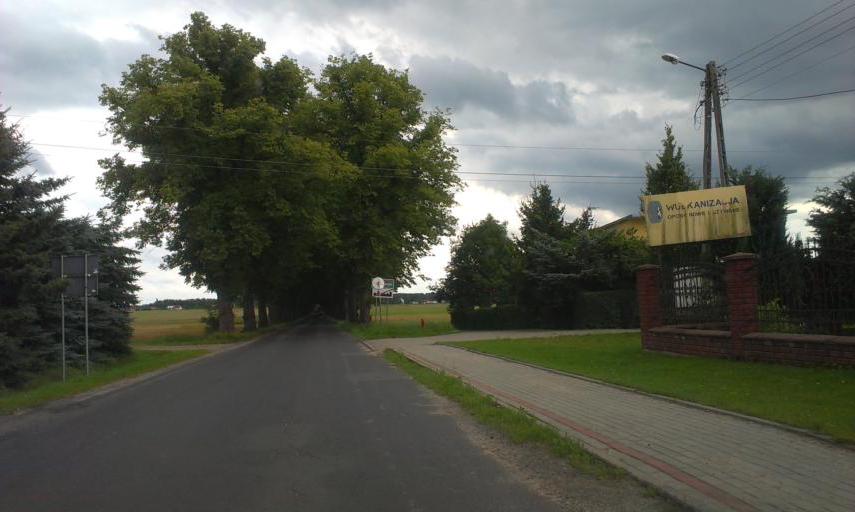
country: PL
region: West Pomeranian Voivodeship
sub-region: Powiat bialogardzki
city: Tychowo
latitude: 53.9361
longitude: 16.2409
